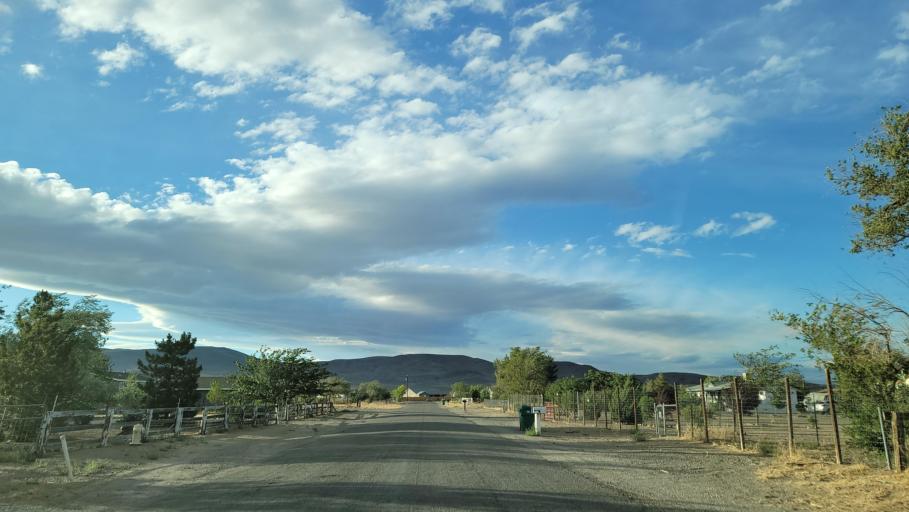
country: US
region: Nevada
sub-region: Lyon County
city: Silver Springs
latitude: 39.3981
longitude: -119.2374
